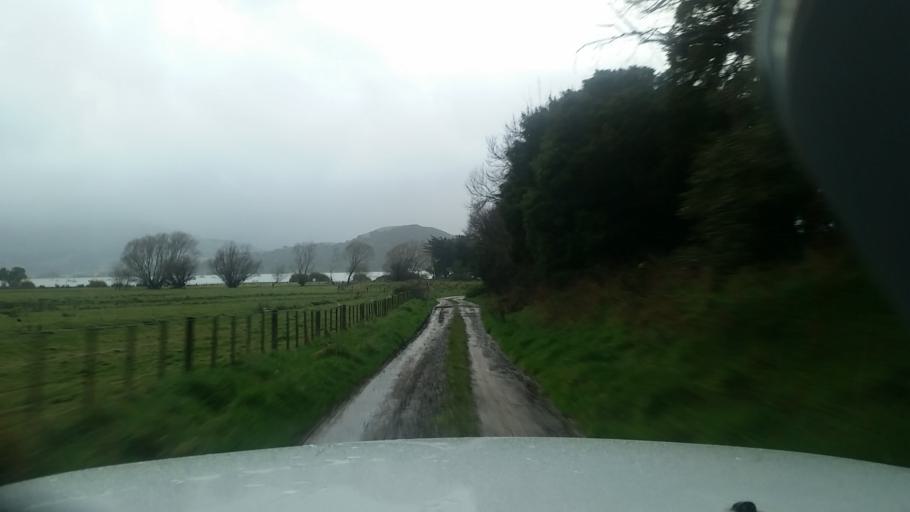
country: NZ
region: Canterbury
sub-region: Christchurch City
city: Christchurch
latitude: -43.7801
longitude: 172.9057
